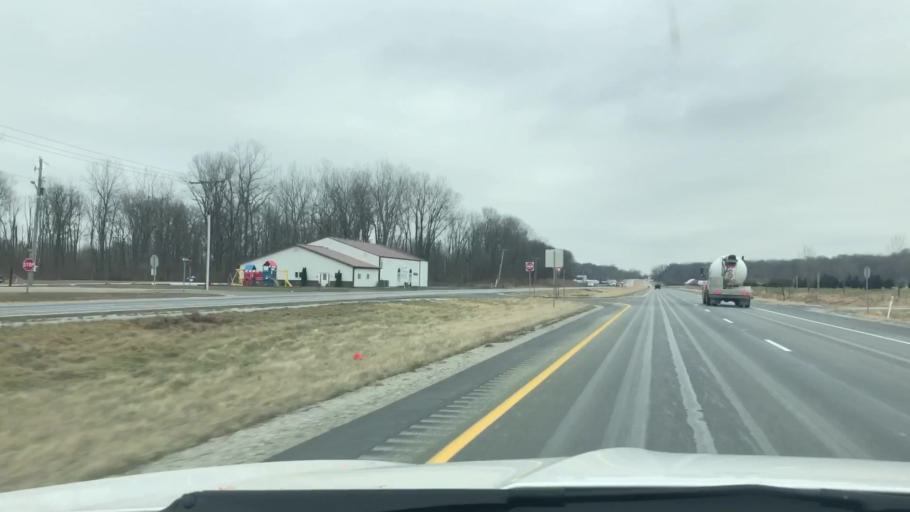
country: US
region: Indiana
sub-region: Cass County
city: Logansport
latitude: 40.7332
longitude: -86.3333
